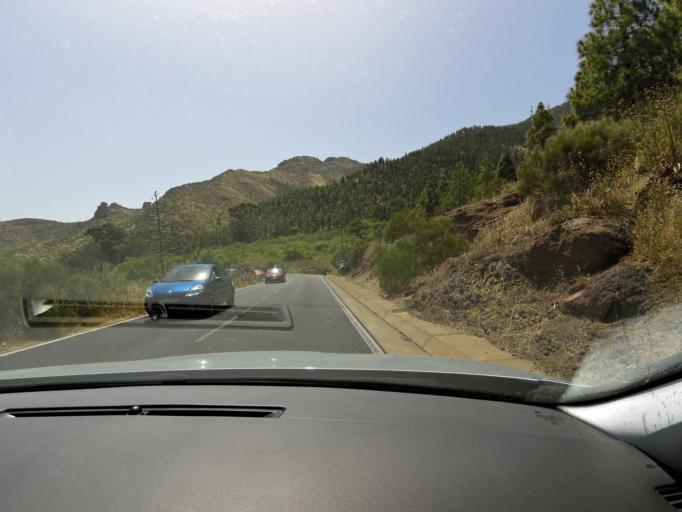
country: ES
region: Canary Islands
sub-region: Provincia de Santa Cruz de Tenerife
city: Santiago del Teide
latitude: 28.3042
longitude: -16.8144
